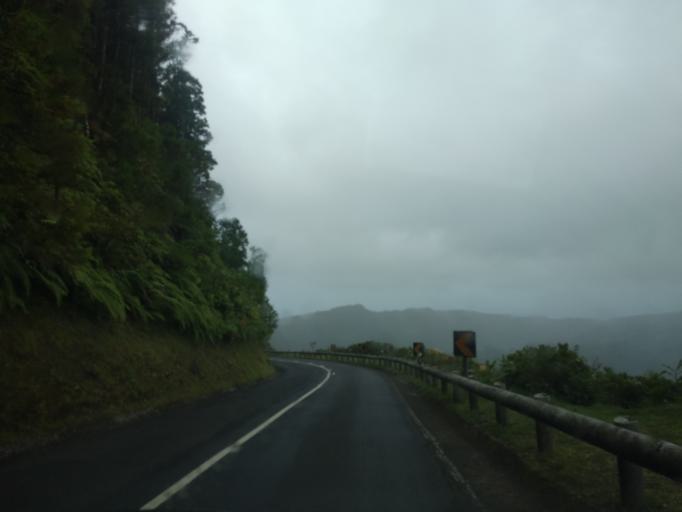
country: PT
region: Azores
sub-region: Ponta Delgada
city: Arrifes
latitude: 37.8382
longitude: -25.7876
